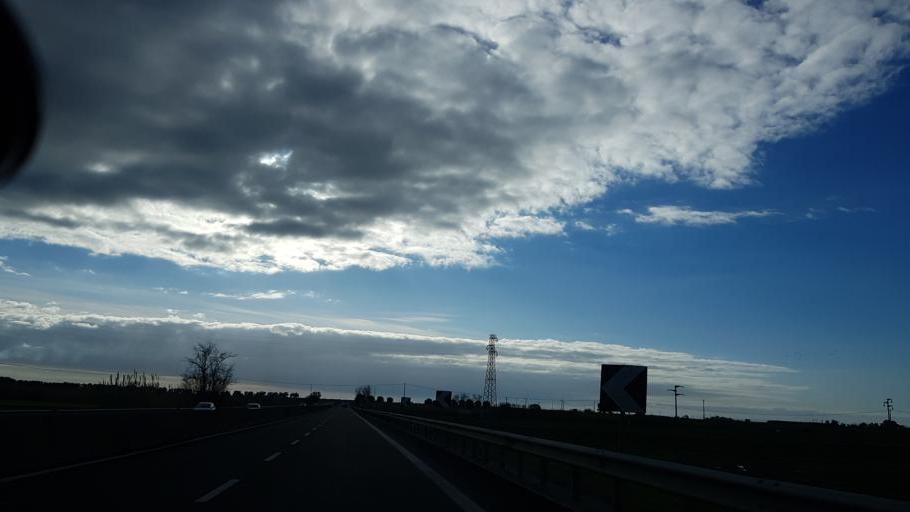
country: IT
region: Apulia
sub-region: Provincia di Brindisi
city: La Rosa
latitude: 40.5986
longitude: 17.9674
